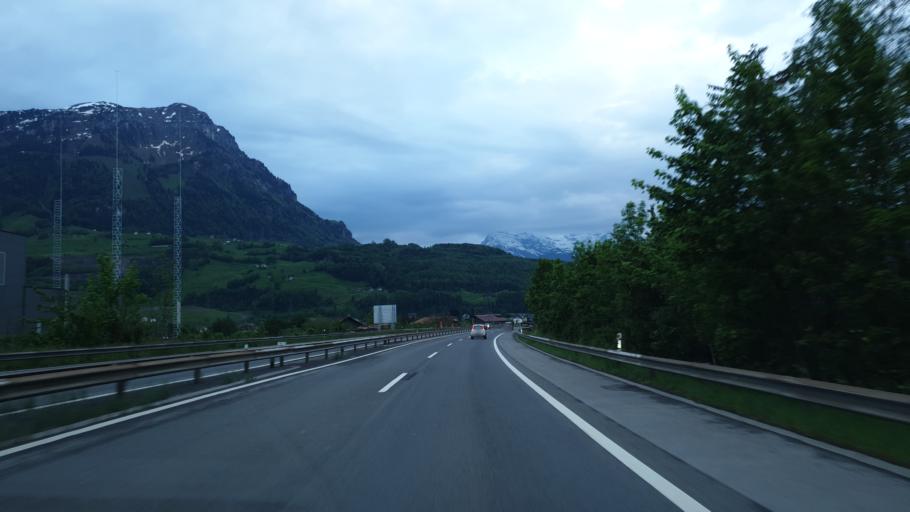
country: CH
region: Schwyz
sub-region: Bezirk Schwyz
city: Ingenbohl
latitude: 47.0142
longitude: 8.6258
